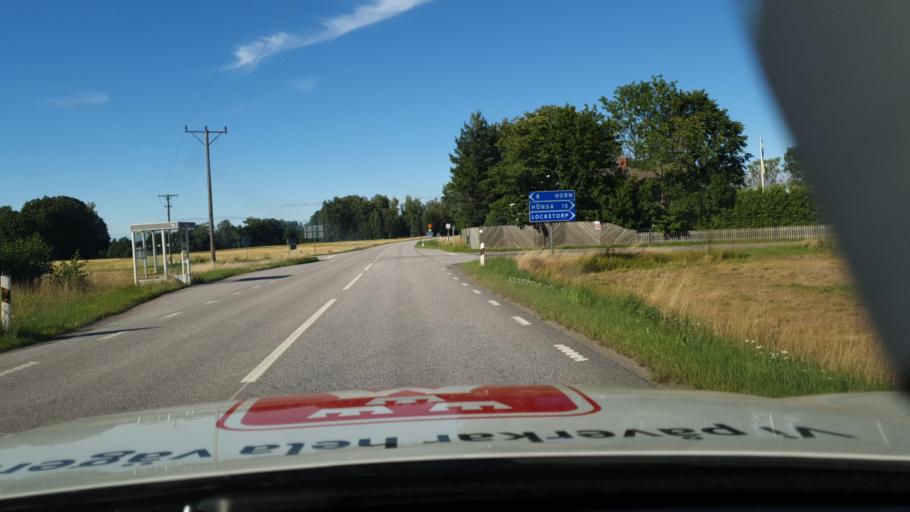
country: SE
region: Vaestra Goetaland
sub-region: Skovde Kommun
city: Stopen
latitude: 58.4876
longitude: 13.9594
